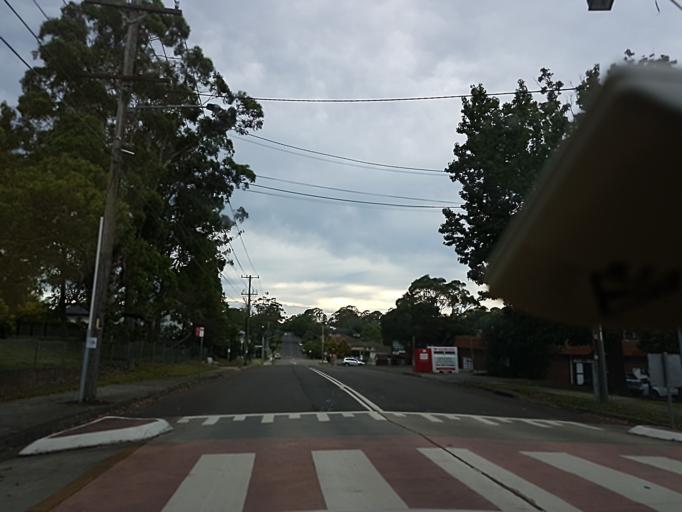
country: AU
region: New South Wales
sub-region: Warringah
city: Davidson
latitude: -33.7283
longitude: 151.2160
